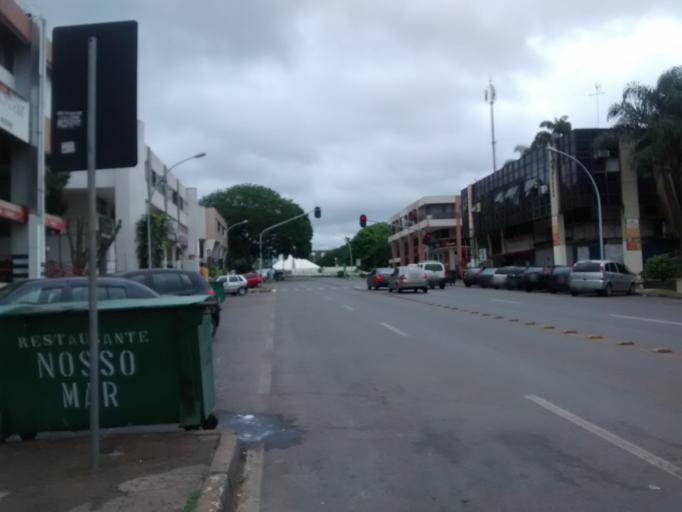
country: BR
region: Federal District
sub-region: Brasilia
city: Brasilia
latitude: -15.7402
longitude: -47.8934
